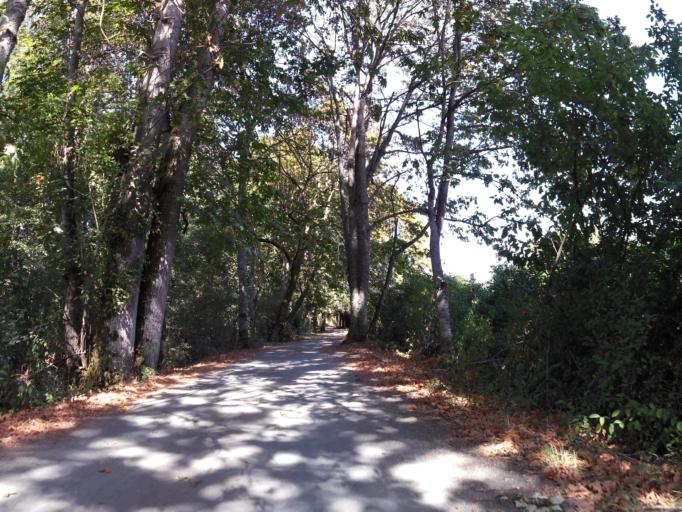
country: CA
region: British Columbia
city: Victoria
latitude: 48.4937
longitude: -123.3605
